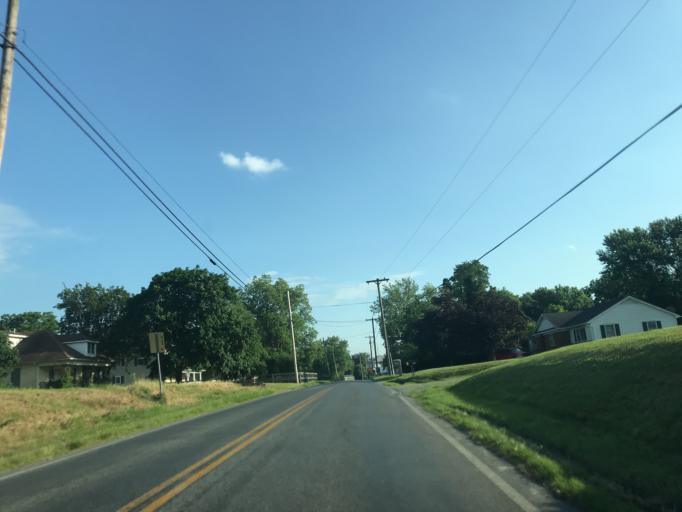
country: US
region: Maryland
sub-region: Caroline County
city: Federalsburg
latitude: 38.7093
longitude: -75.7765
